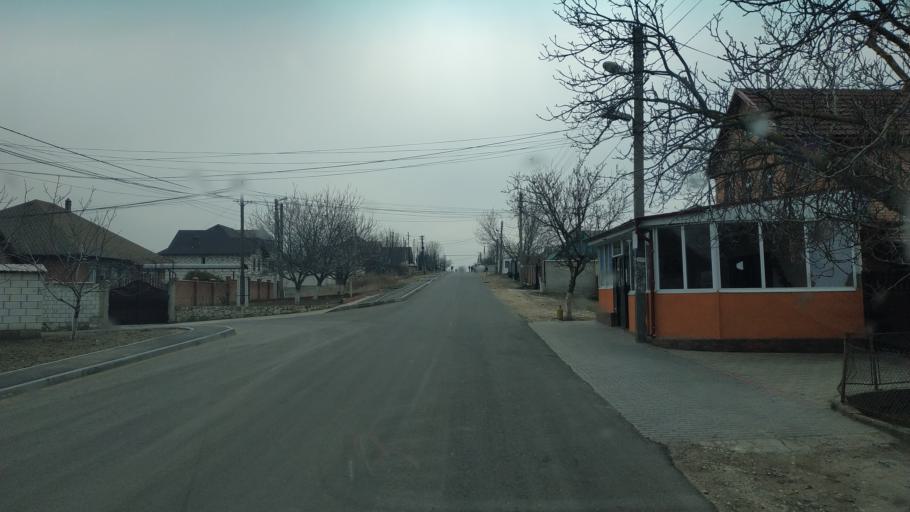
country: MD
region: Chisinau
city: Singera
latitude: 46.9078
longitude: 28.9870
